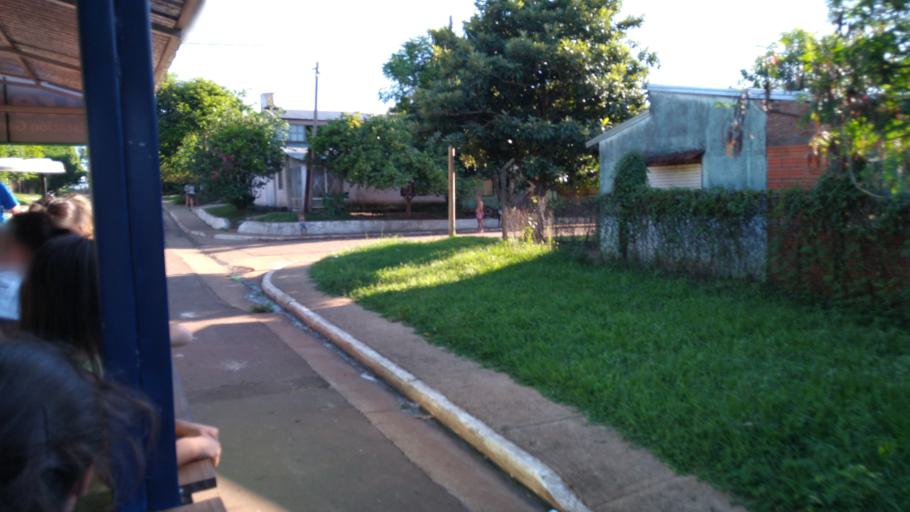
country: AR
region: Misiones
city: Garupa
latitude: -27.4893
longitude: -55.8208
